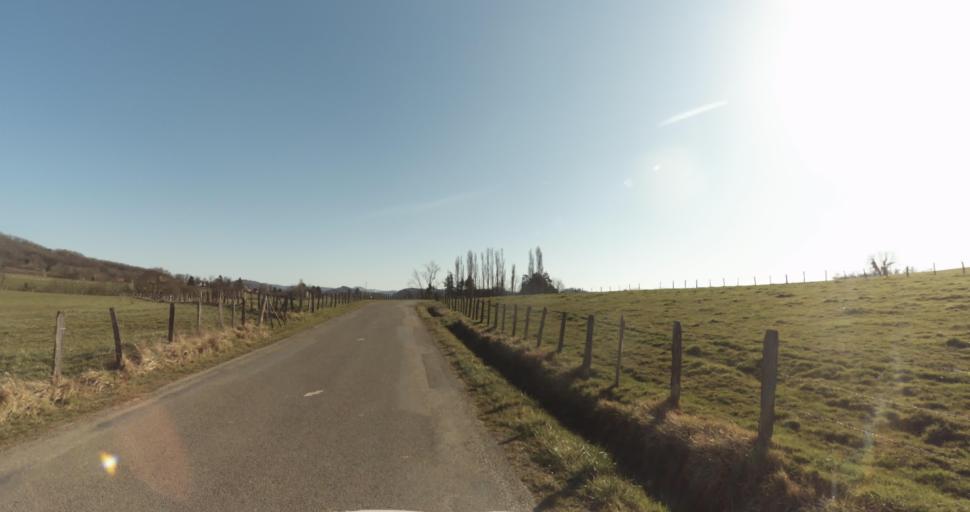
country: FR
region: Franche-Comte
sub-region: Departement du Jura
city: Montmorot
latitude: 46.6941
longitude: 5.5330
